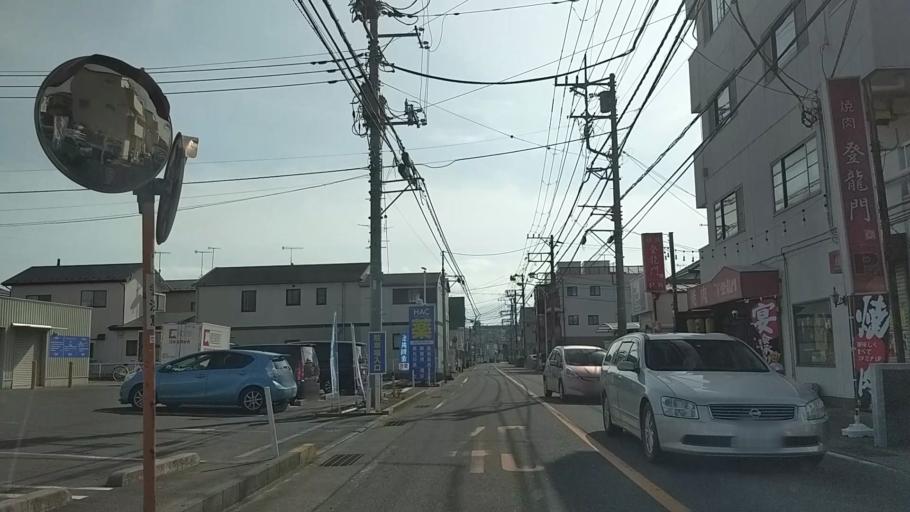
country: JP
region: Kanagawa
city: Chigasaki
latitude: 35.3378
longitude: 139.3830
